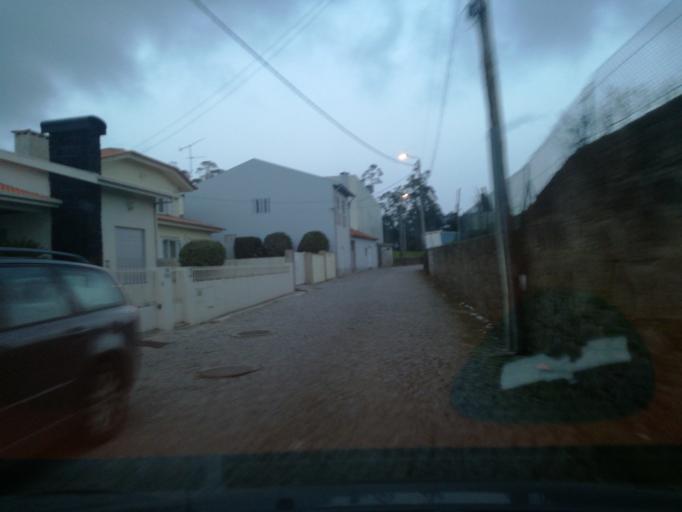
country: PT
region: Porto
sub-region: Maia
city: Gemunde
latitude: 41.2682
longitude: -8.6551
